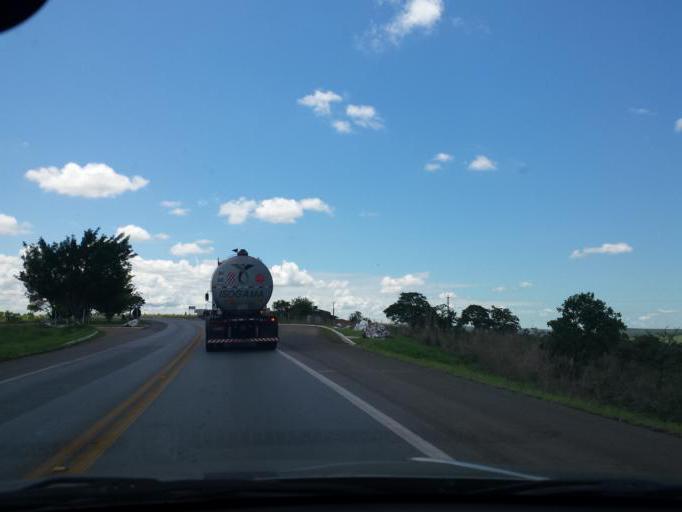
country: BR
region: Goias
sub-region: Cristalina
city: Cristalina
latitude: -16.5655
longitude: -47.7915
